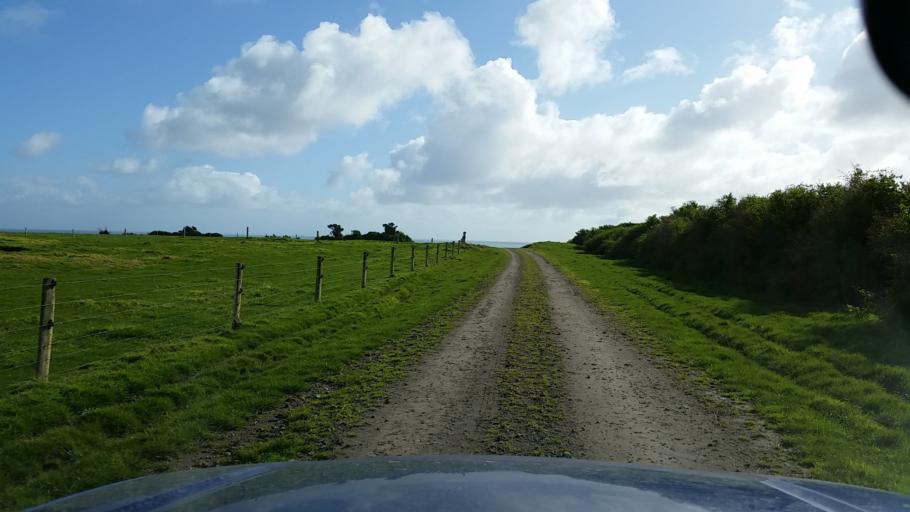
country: NZ
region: Taranaki
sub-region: South Taranaki District
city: Hawera
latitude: -39.6588
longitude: 174.3589
